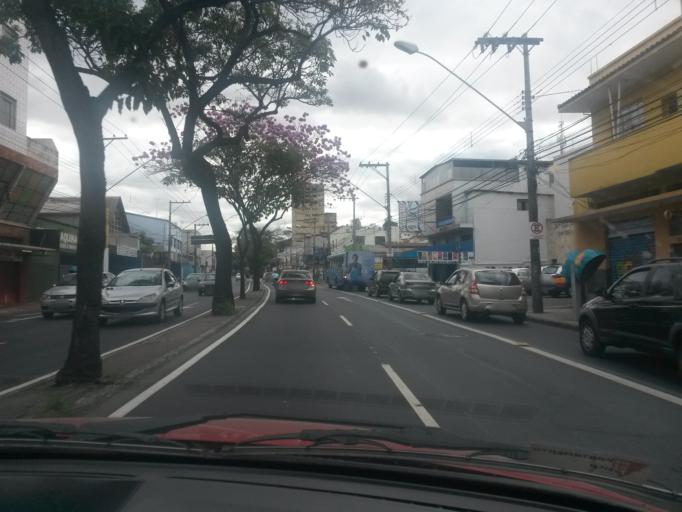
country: BR
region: Minas Gerais
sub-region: Belo Horizonte
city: Belo Horizonte
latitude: -19.9080
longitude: -43.9614
